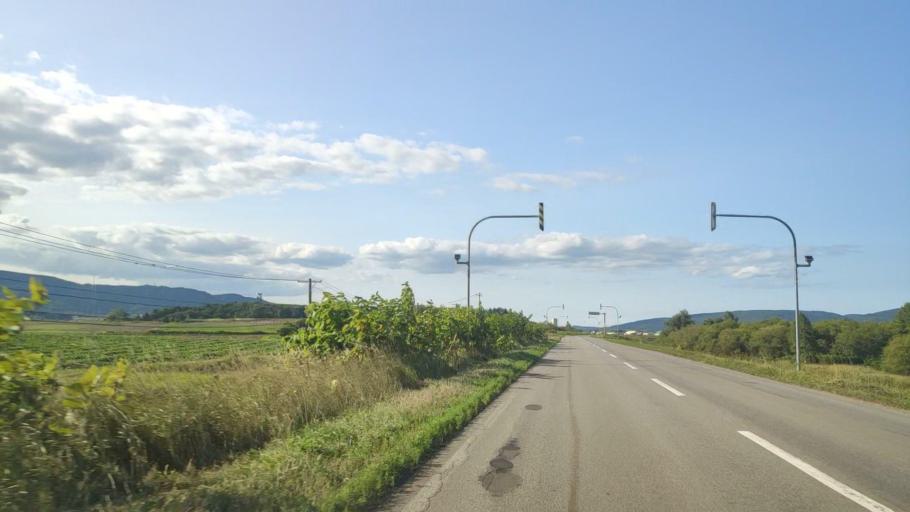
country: JP
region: Hokkaido
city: Nayoro
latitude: 44.8088
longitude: 142.0665
